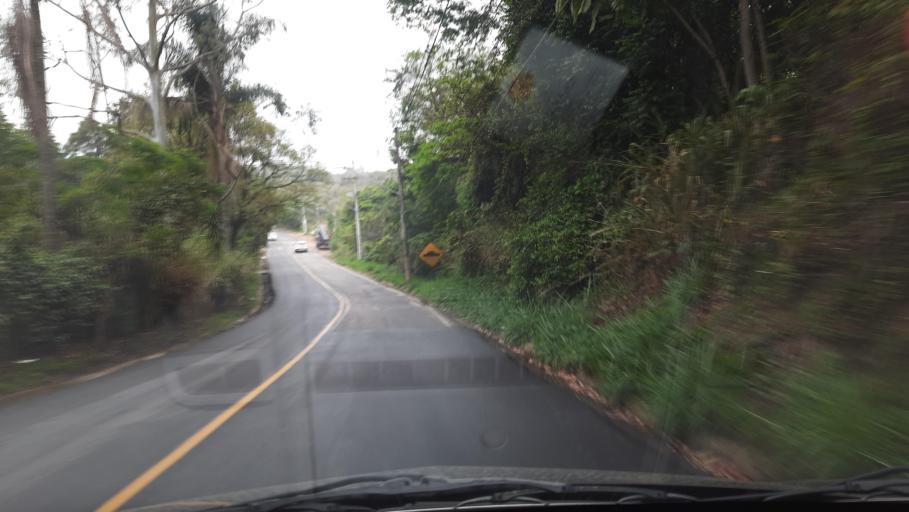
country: BR
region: Sao Paulo
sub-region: Caieiras
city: Caieiras
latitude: -23.3735
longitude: -46.6946
